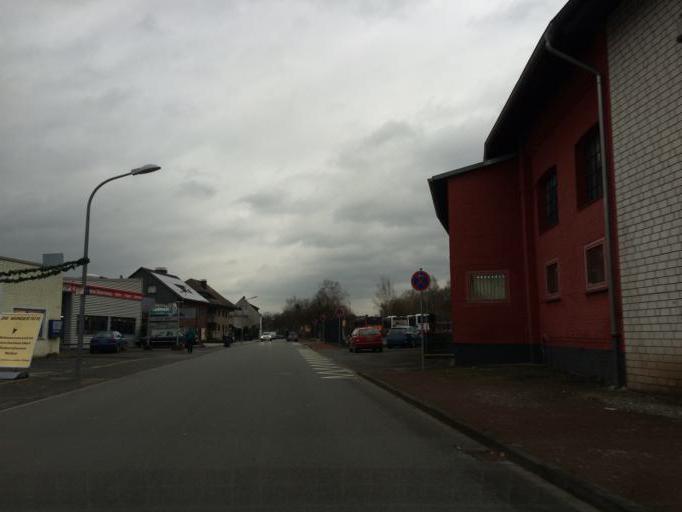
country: DE
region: North Rhine-Westphalia
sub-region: Regierungsbezirk Munster
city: Haltern
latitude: 51.7365
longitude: 7.1783
